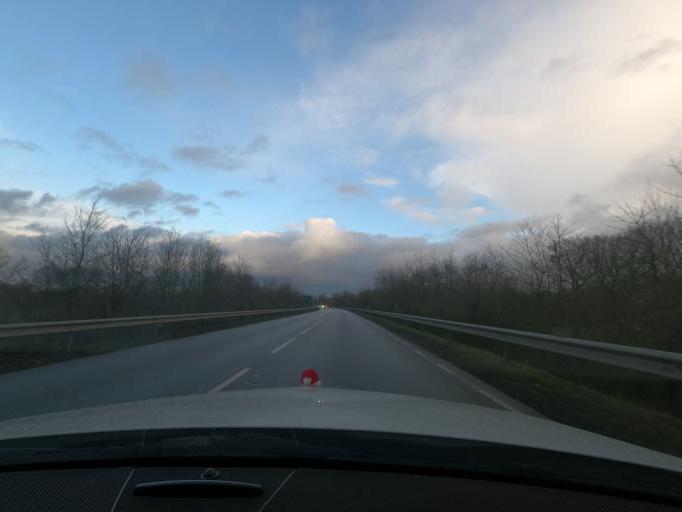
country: DE
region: Schleswig-Holstein
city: Alveslohe
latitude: 53.8044
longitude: 9.9333
